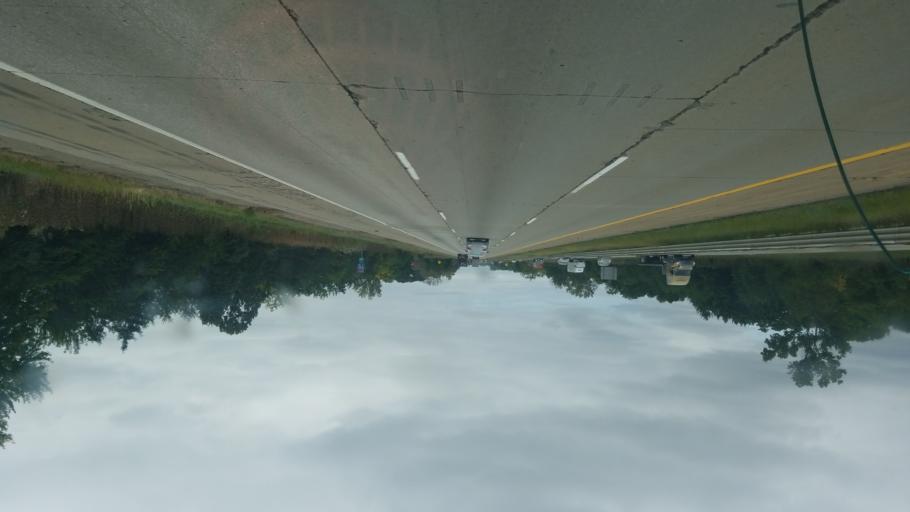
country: US
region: Michigan
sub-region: Monroe County
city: Luna Pier
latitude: 41.7327
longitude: -83.4885
